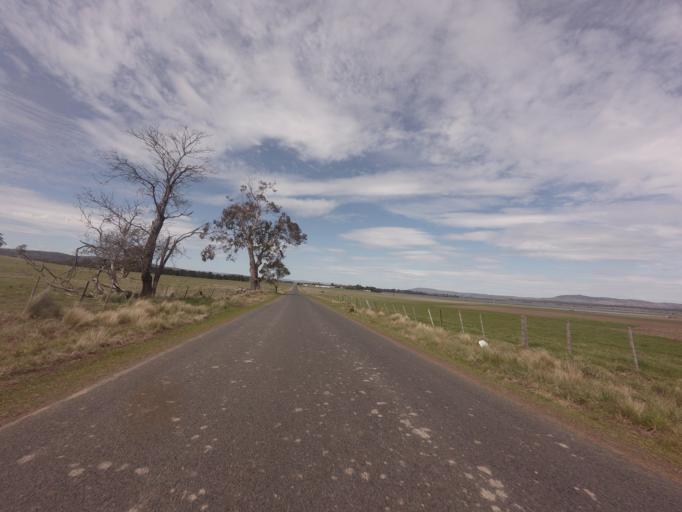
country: AU
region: Tasmania
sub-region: Northern Midlands
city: Evandale
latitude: -41.8060
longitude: 147.2764
